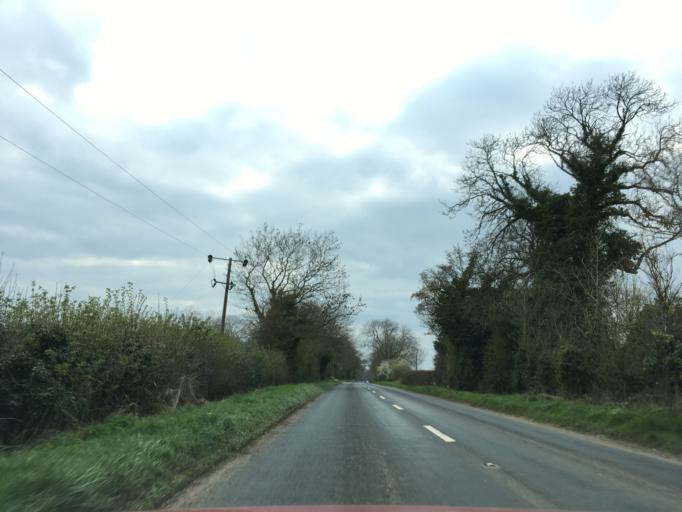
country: GB
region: England
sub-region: Gloucestershire
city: Bourton on the Water
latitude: 51.7888
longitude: -1.7233
